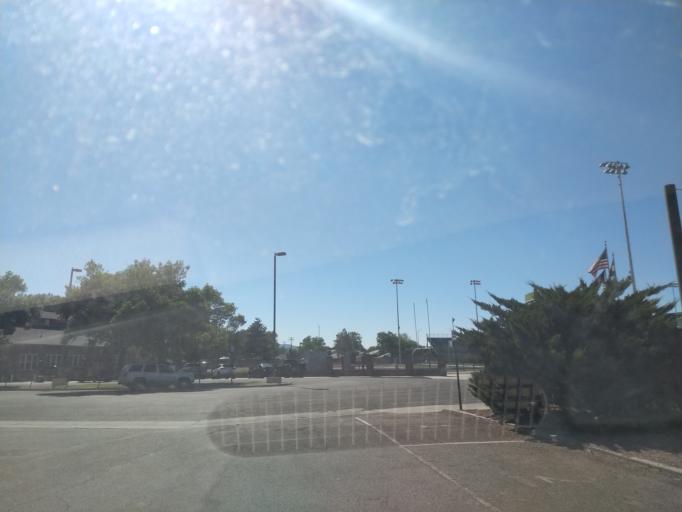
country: US
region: Colorado
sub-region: Mesa County
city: Grand Junction
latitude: 39.0757
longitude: -108.5504
